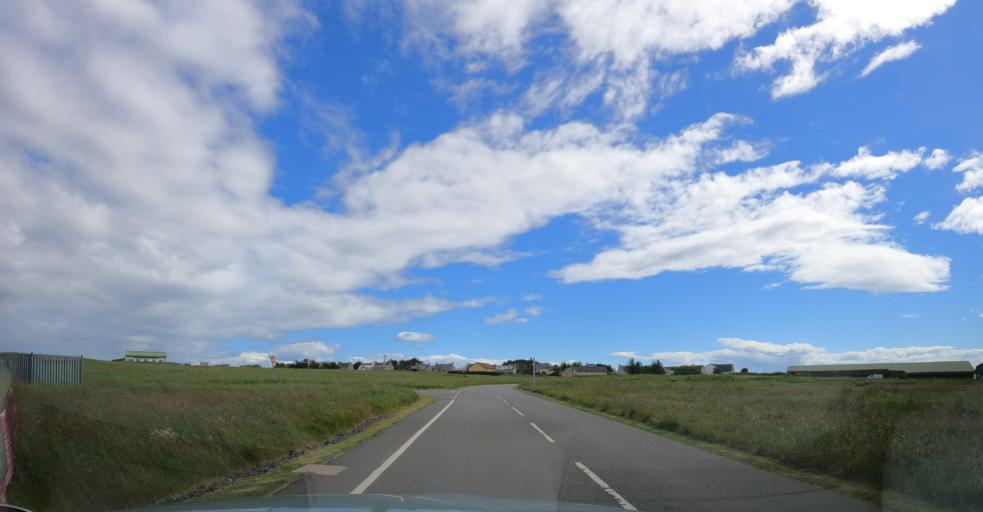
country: GB
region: Scotland
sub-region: Eilean Siar
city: Stornoway
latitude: 58.2125
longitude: -6.3224
